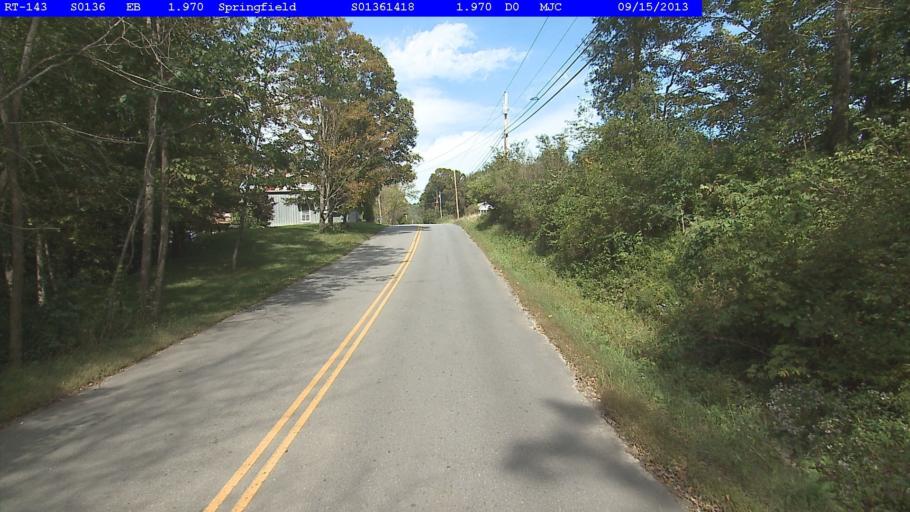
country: US
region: Vermont
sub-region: Windsor County
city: Springfield
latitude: 43.2930
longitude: -72.4500
